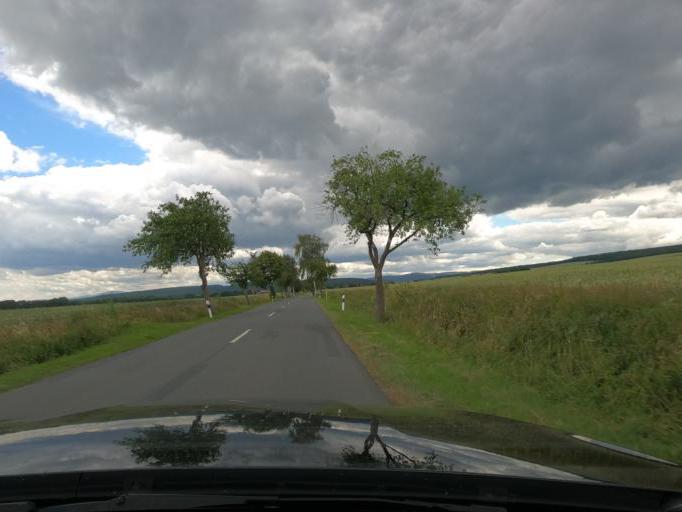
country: DE
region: Lower Saxony
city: Heere
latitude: 52.0542
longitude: 10.2557
